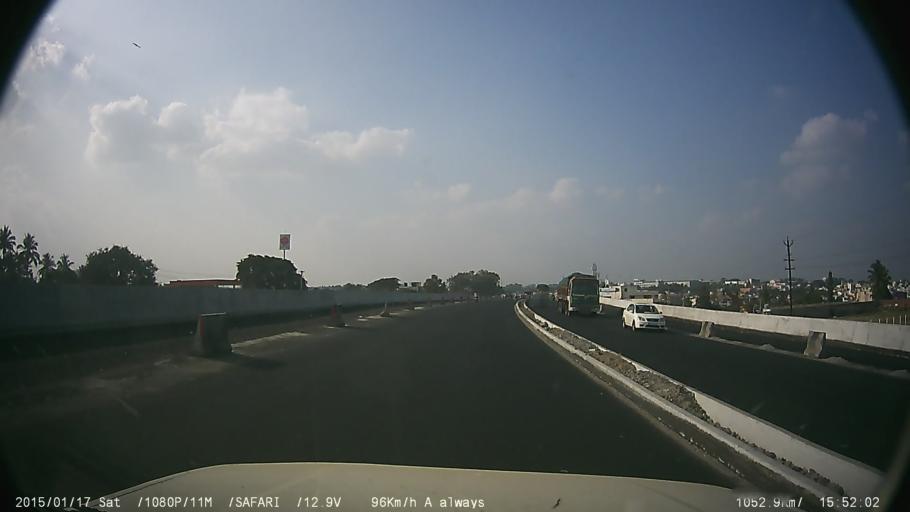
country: IN
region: Tamil Nadu
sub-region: Krishnagiri
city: Hosur
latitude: 12.7383
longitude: 77.8219
